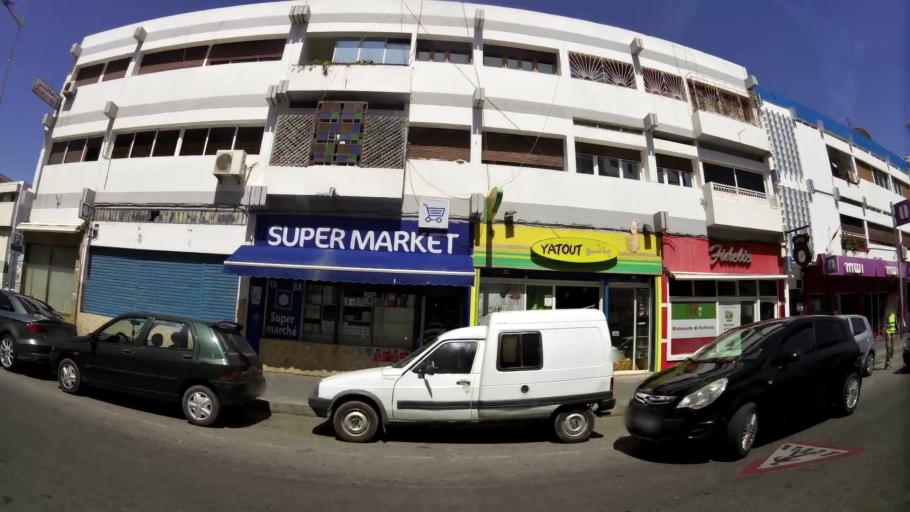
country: MA
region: Souss-Massa-Draa
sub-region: Agadir-Ida-ou-Tnan
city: Agadir
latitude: 30.4137
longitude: -9.5937
